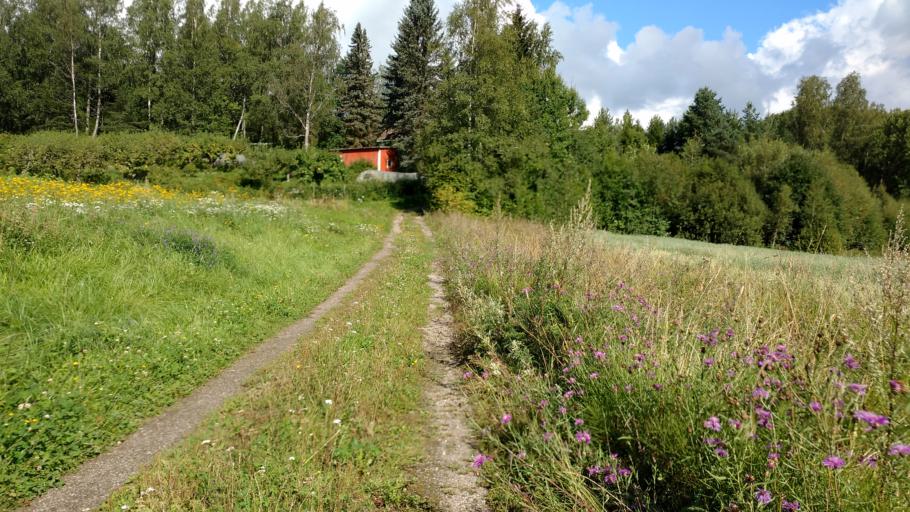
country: FI
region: Varsinais-Suomi
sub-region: Salo
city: Salo
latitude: 60.3528
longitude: 23.1355
